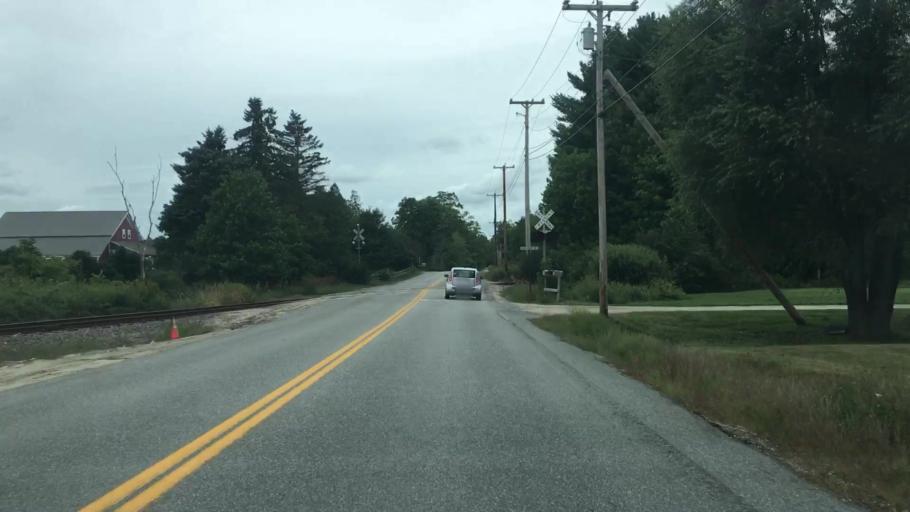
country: US
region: Maine
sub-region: Cumberland County
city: Yarmouth
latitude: 43.8404
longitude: -70.2083
